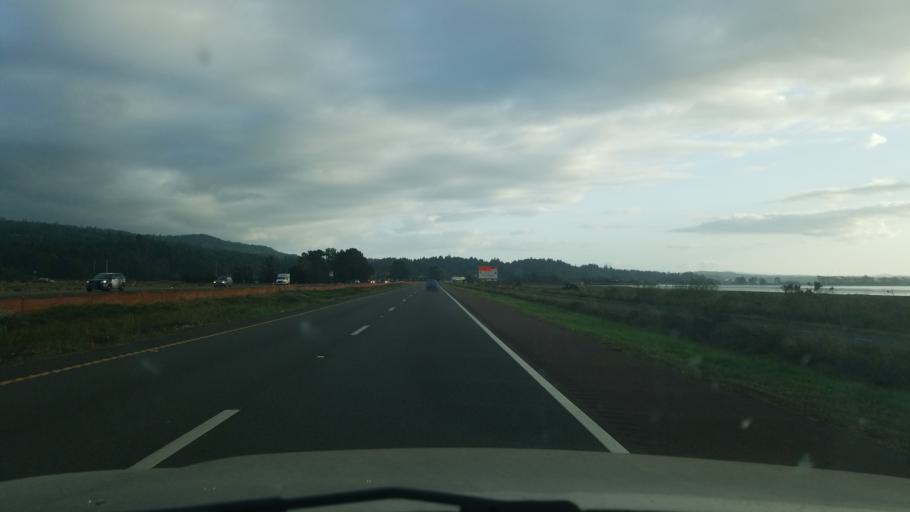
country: US
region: California
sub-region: Humboldt County
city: Bayside
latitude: 40.8401
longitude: -124.0822
